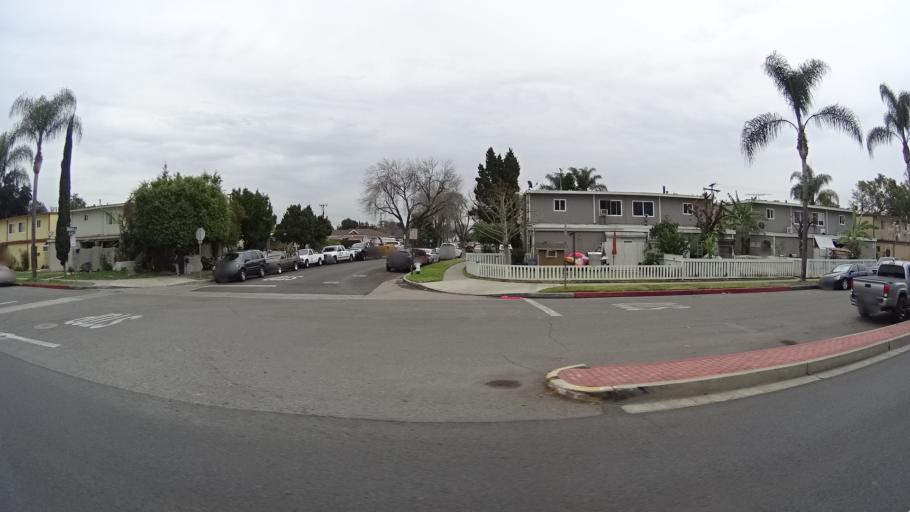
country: US
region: California
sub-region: Orange County
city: Fountain Valley
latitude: 33.7176
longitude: -117.9078
